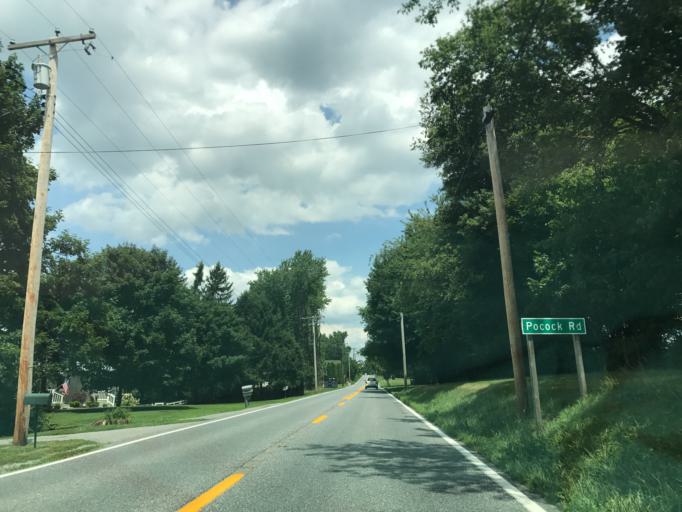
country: US
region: Maryland
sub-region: Harford County
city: Jarrettsville
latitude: 39.5747
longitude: -76.5181
